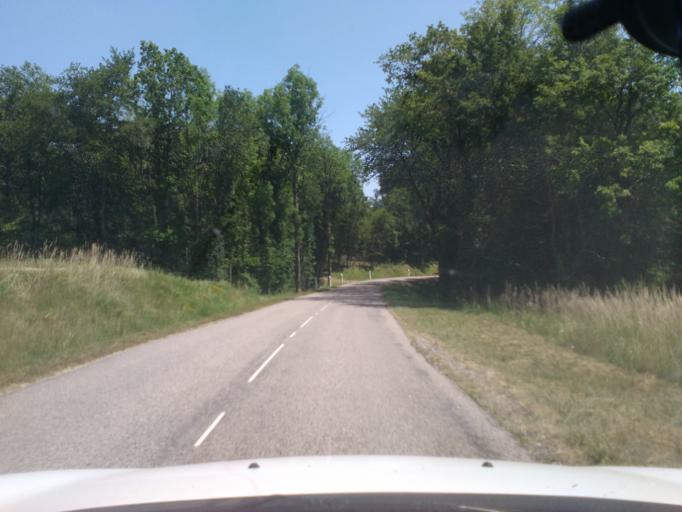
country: FR
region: Lorraine
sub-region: Departement des Vosges
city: Liffol-le-Grand
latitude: 48.4133
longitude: 5.5823
